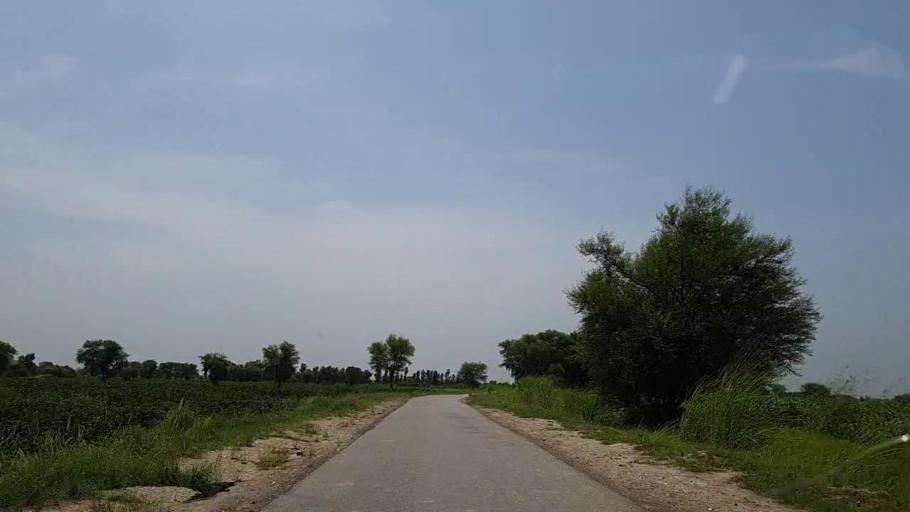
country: PK
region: Sindh
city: Khanpur
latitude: 27.8959
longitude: 69.4966
